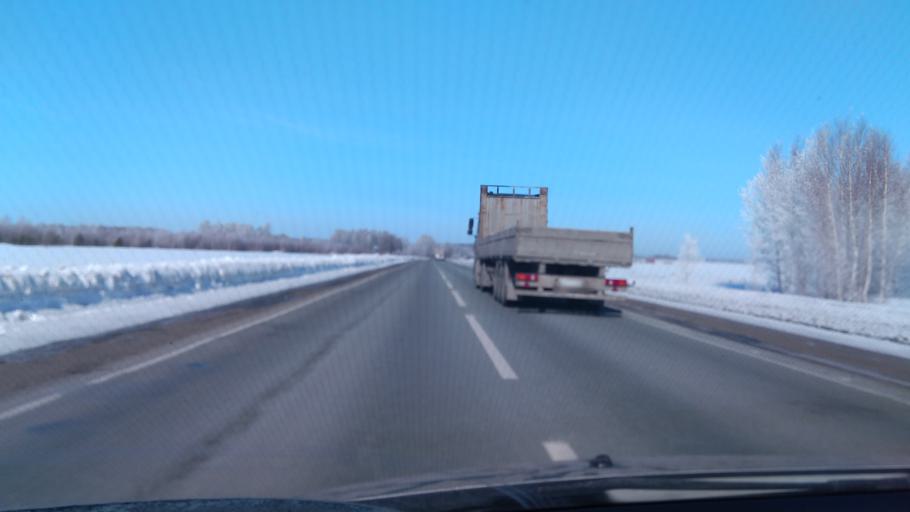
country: RU
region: Perm
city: Suksun
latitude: 56.9366
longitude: 57.5408
